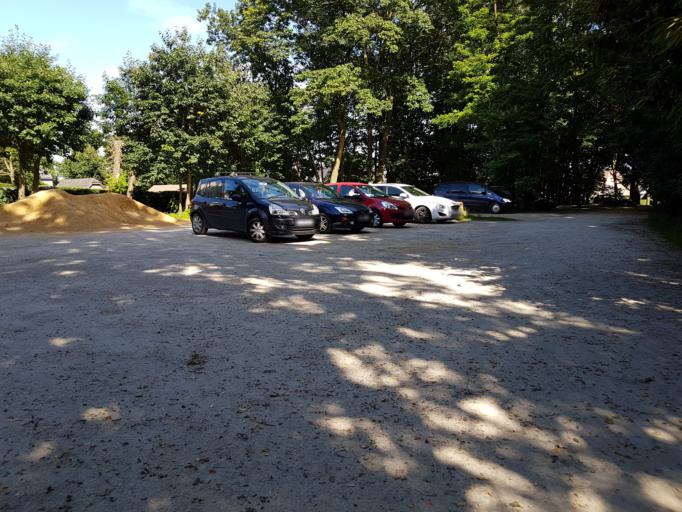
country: BE
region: Flanders
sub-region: Provincie Antwerpen
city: Mechelen
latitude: 51.0478
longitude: 4.4754
